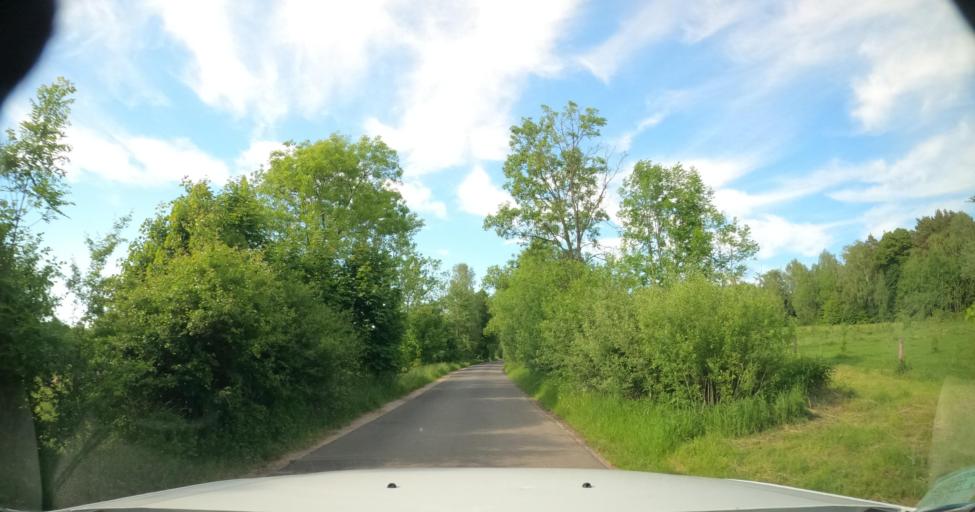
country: PL
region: Warmian-Masurian Voivodeship
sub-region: Powiat ostrodzki
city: Morag
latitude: 54.0691
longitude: 19.8899
